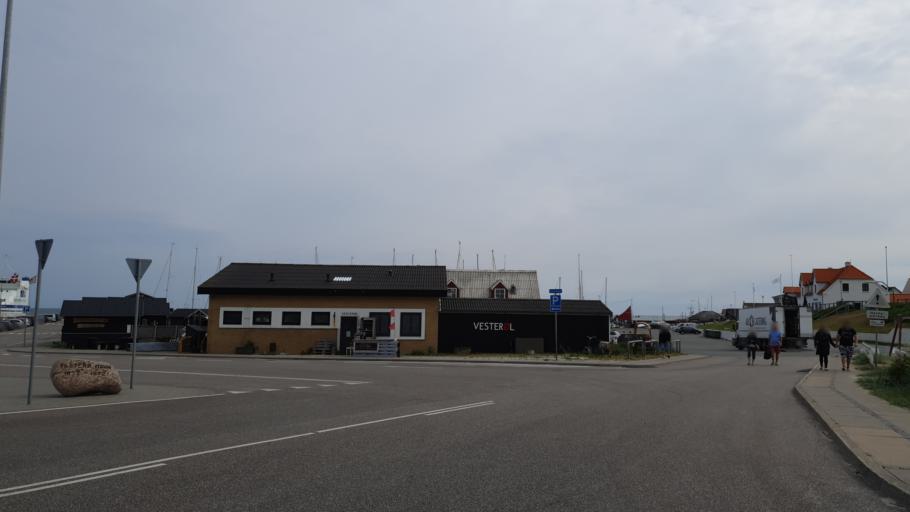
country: DK
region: North Denmark
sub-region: Laeso Kommune
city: Byrum
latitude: 57.2945
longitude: 10.9228
